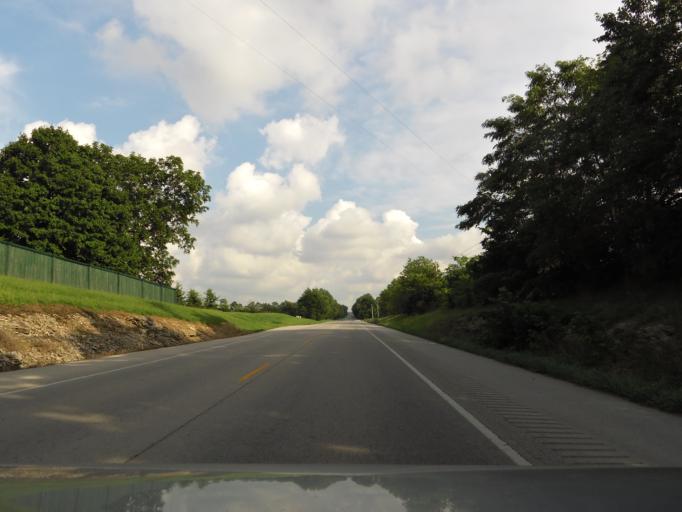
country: US
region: Kentucky
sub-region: Bourbon County
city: Paris
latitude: 38.2575
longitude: -84.2924
